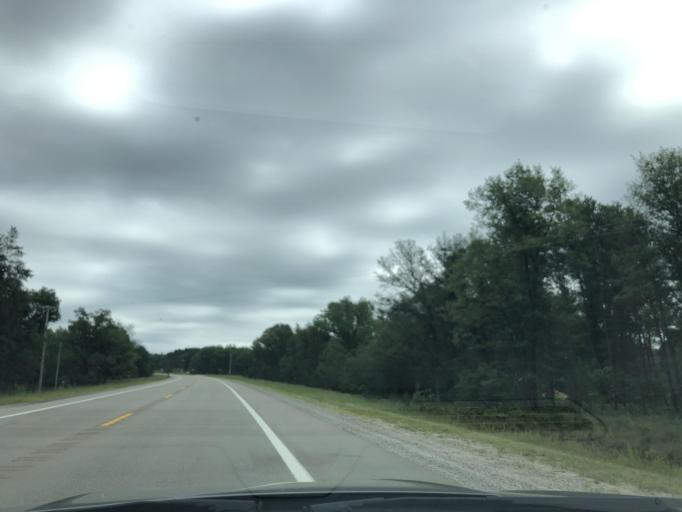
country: US
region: Michigan
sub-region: Clare County
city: Harrison
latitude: 44.0323
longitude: -85.0219
